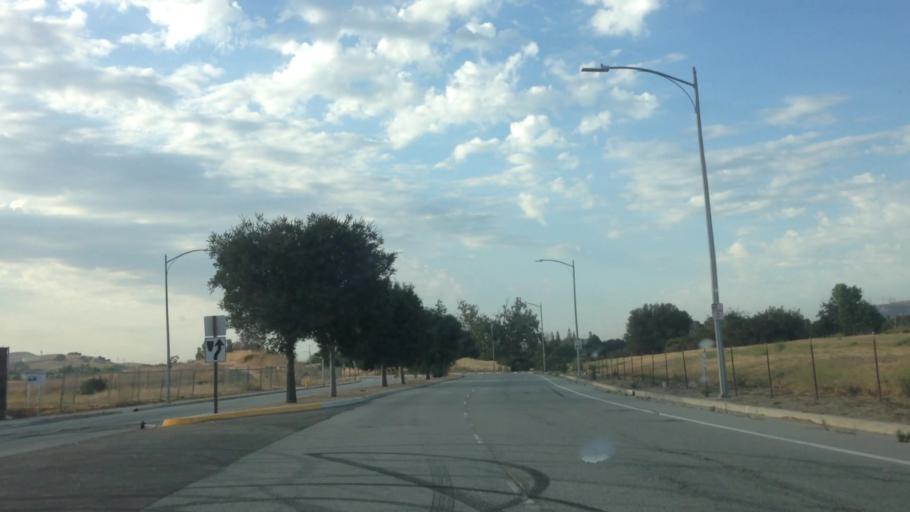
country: US
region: California
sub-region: Santa Clara County
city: Seven Trees
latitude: 37.2551
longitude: -121.7774
